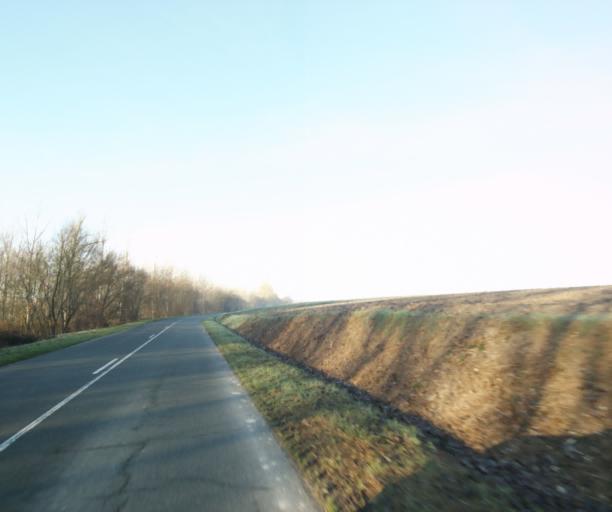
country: FR
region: Poitou-Charentes
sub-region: Departement de la Charente-Maritime
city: Cherac
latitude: 45.6854
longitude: -0.4401
